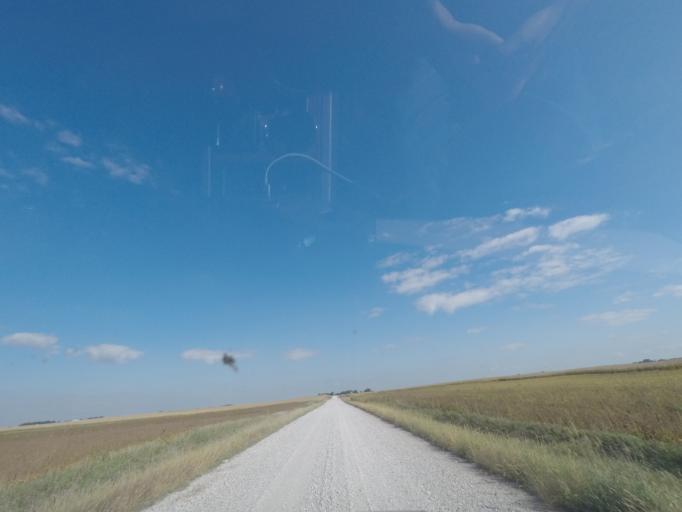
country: US
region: Iowa
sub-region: Story County
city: Nevada
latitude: 42.0469
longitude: -93.4252
